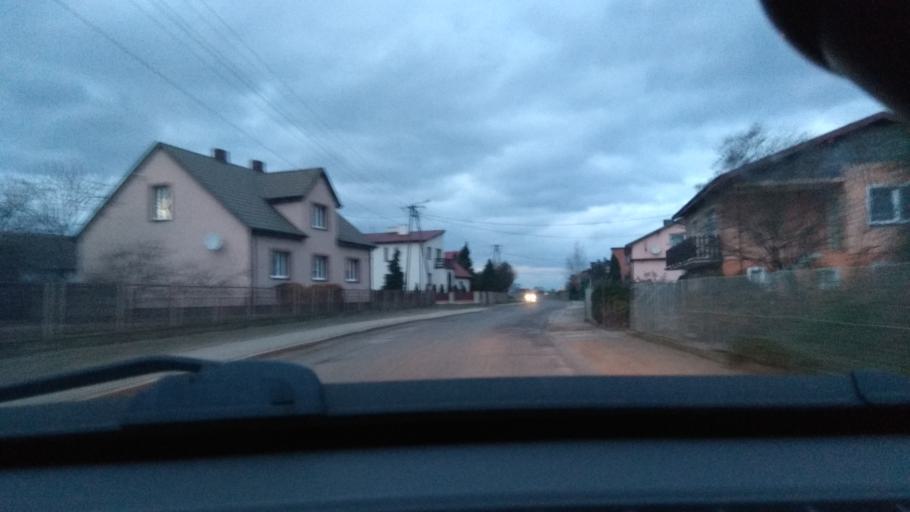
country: PL
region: Lodz Voivodeship
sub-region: Powiat wieruszowski
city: Wieruszow
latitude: 51.3063
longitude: 18.0816
